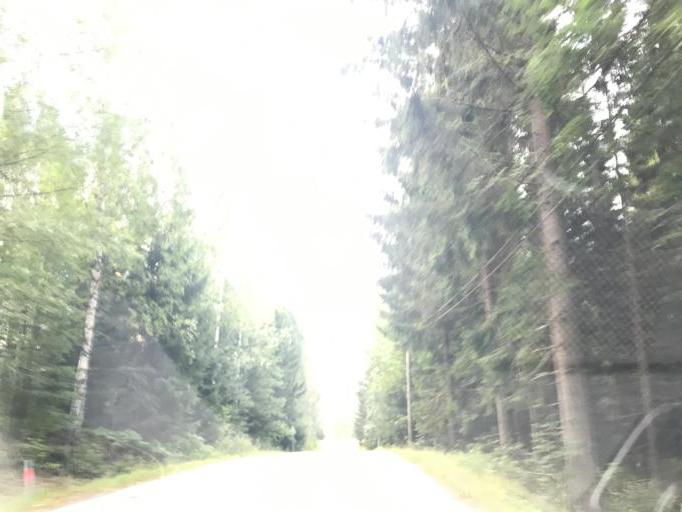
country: FI
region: Uusimaa
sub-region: Helsinki
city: Vihti
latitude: 60.3907
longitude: 24.5167
